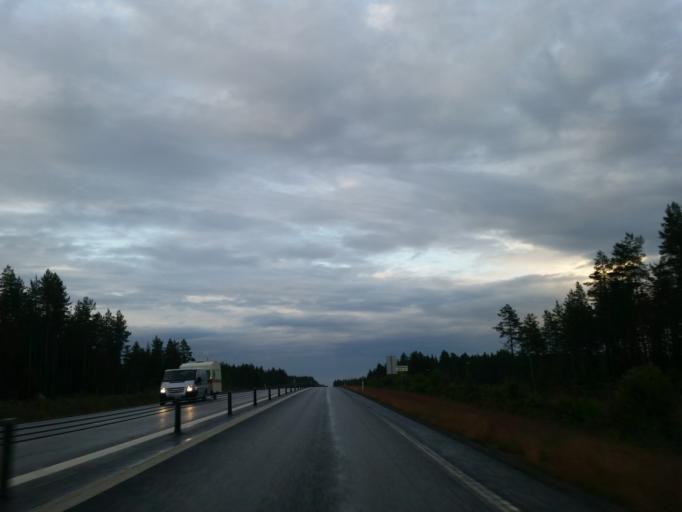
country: SE
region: Vaesterbotten
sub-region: Umea Kommun
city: Taftea
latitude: 63.8735
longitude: 20.4615
